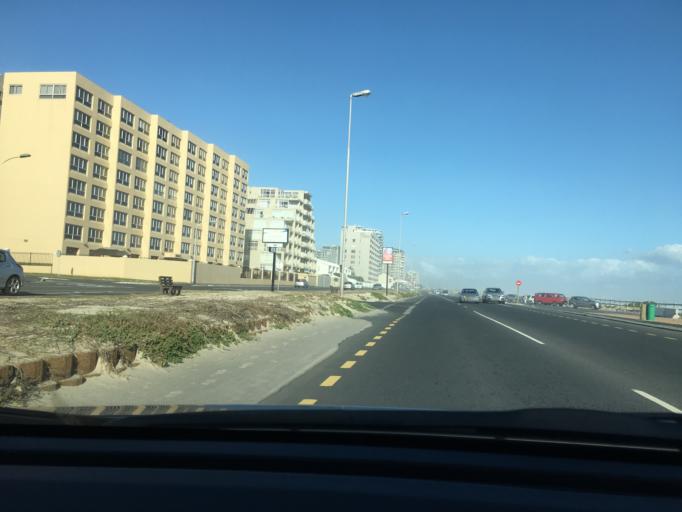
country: ZA
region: Western Cape
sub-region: City of Cape Town
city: Sunset Beach
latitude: -33.8178
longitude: 18.4740
